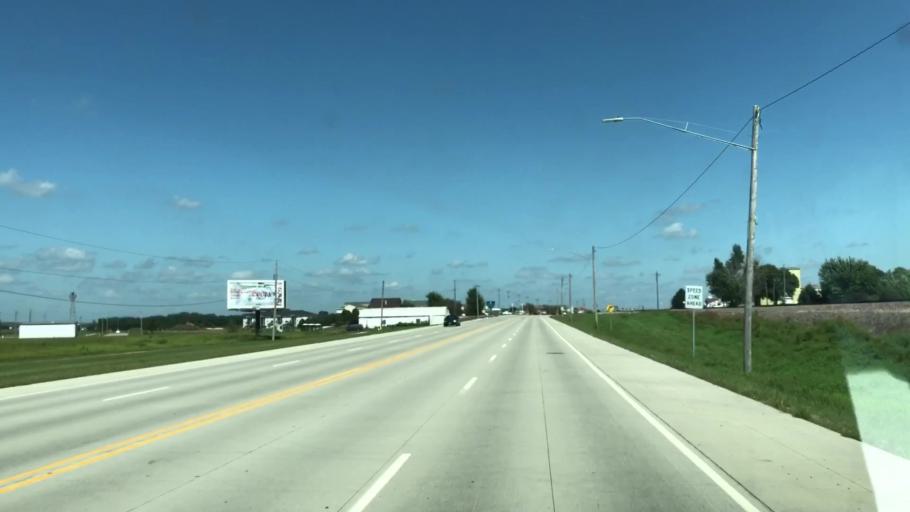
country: US
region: Iowa
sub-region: Plymouth County
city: Le Mars
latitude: 42.7735
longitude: -96.1914
